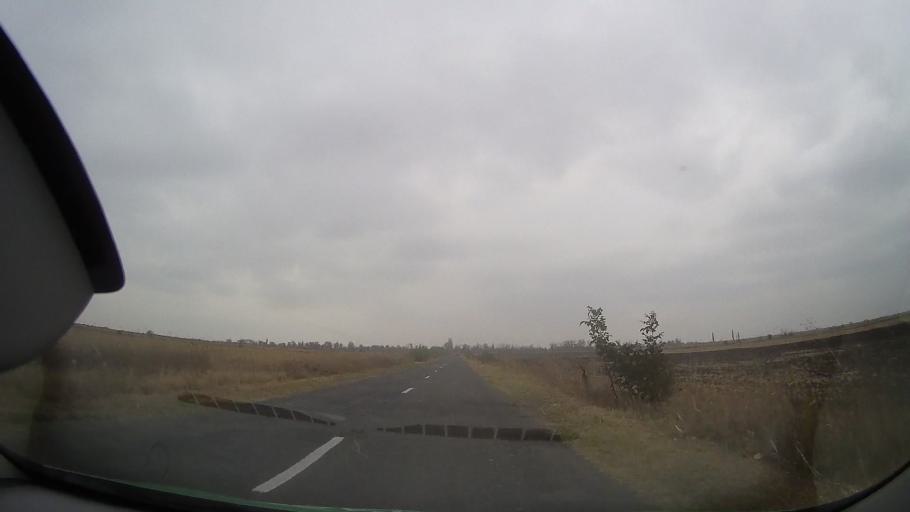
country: RO
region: Ialomita
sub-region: Comuna Garbovi
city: Garbovi
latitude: 44.7660
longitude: 26.7931
